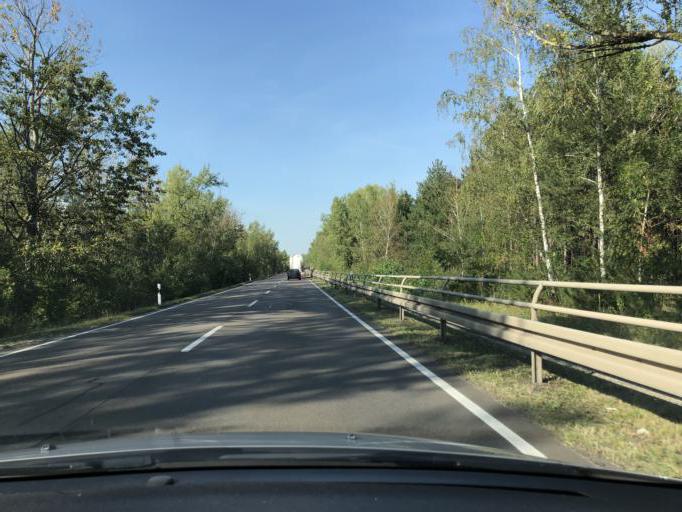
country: DE
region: Saxony-Anhalt
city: Grosskayna
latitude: 51.2965
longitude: 11.9168
